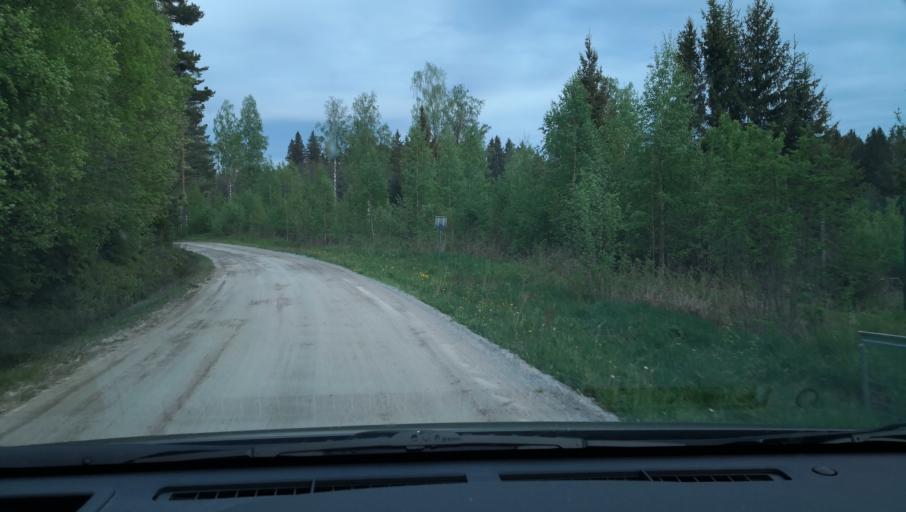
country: SE
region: Vaestmanland
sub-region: Skinnskattebergs Kommun
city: Skinnskatteberg
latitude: 59.7329
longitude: 15.4724
